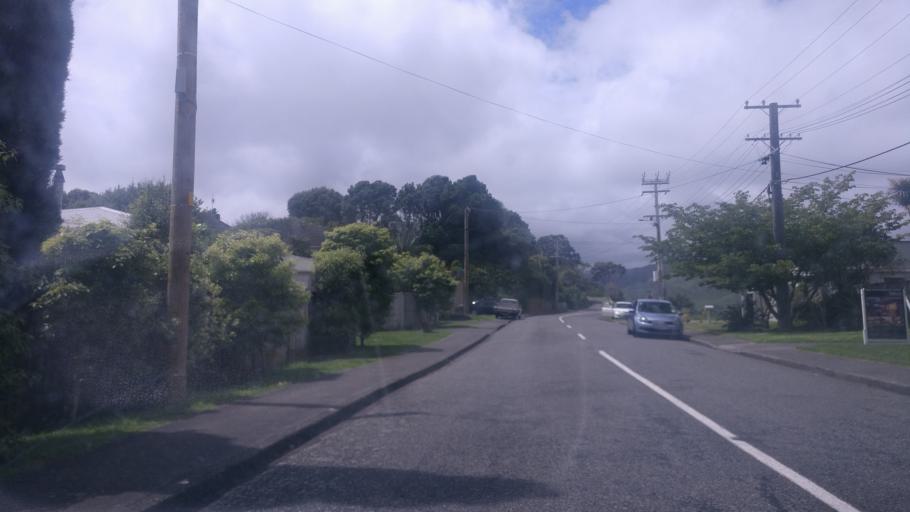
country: NZ
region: Wellington
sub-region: Kapiti Coast District
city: Paraparaumu
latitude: -40.9836
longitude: 174.9582
